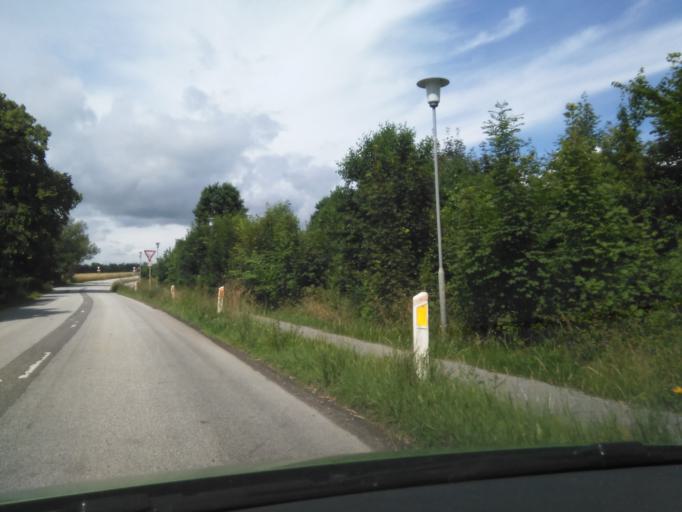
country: DK
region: Central Jutland
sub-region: Arhus Kommune
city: Logten
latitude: 56.2545
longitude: 10.3367
